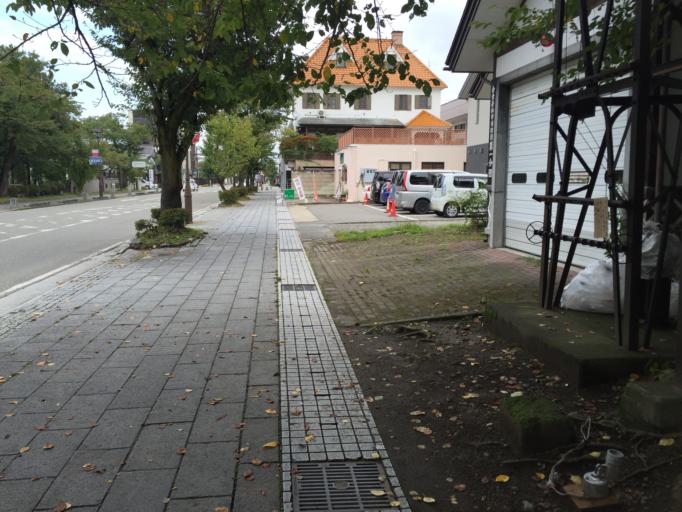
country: JP
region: Fukushima
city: Kitakata
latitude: 37.4906
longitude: 139.9305
